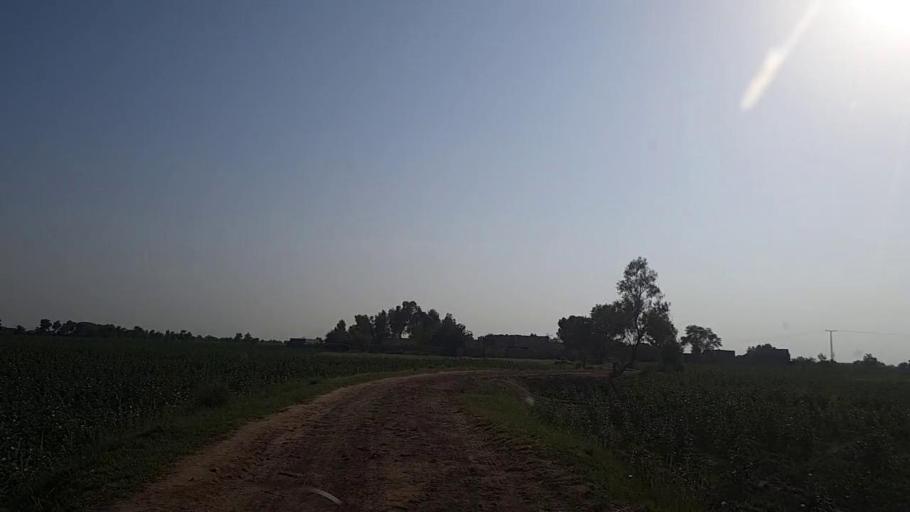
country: PK
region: Sindh
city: Khanpur
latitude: 27.7305
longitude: 69.3155
